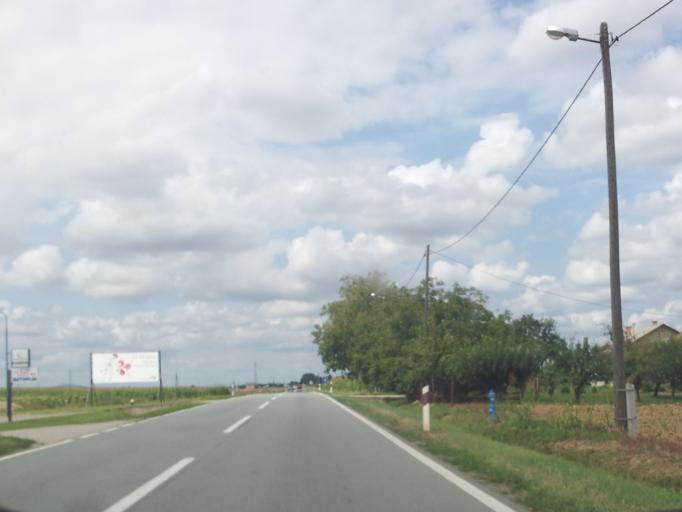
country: HR
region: Osjecko-Baranjska
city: Beli Manastir
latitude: 45.7509
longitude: 18.6397
